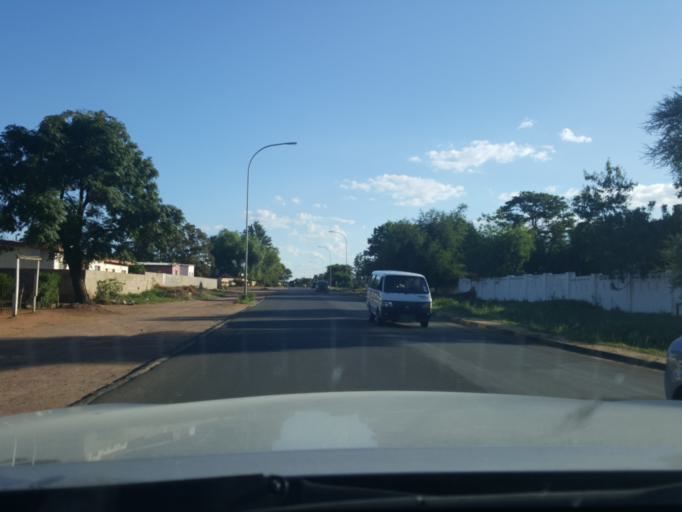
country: BW
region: South East
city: Gaborone
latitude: -24.6289
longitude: 25.9423
